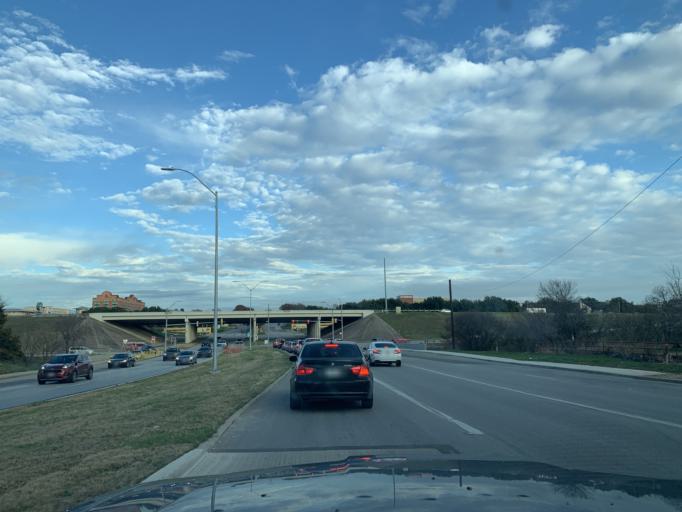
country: US
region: Texas
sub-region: Tarrant County
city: Euless
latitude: 32.8221
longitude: -97.0632
